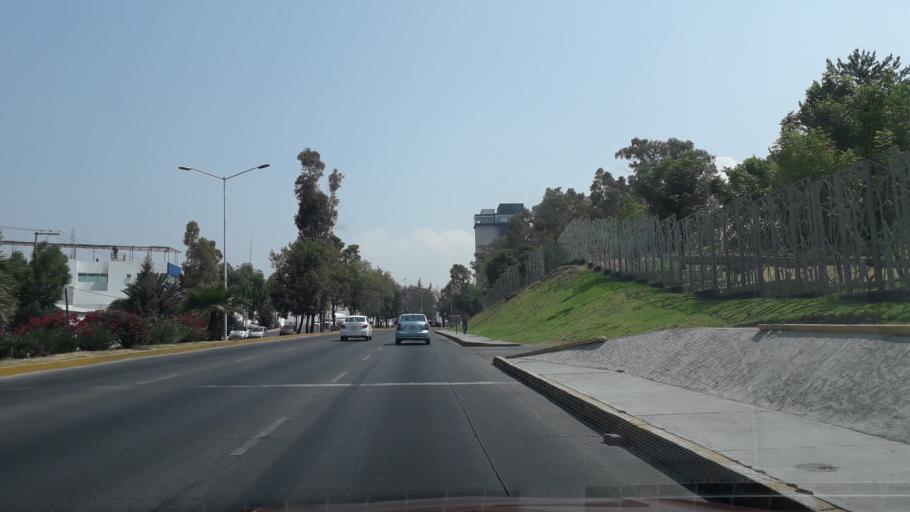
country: MX
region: Puebla
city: Puebla
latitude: 19.0578
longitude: -98.1887
